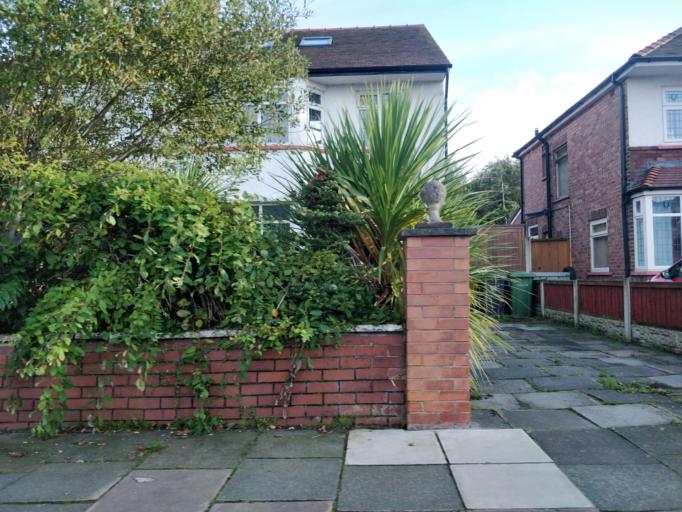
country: GB
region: England
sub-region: Lancashire
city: Banks
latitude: 53.6640
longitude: -2.9605
